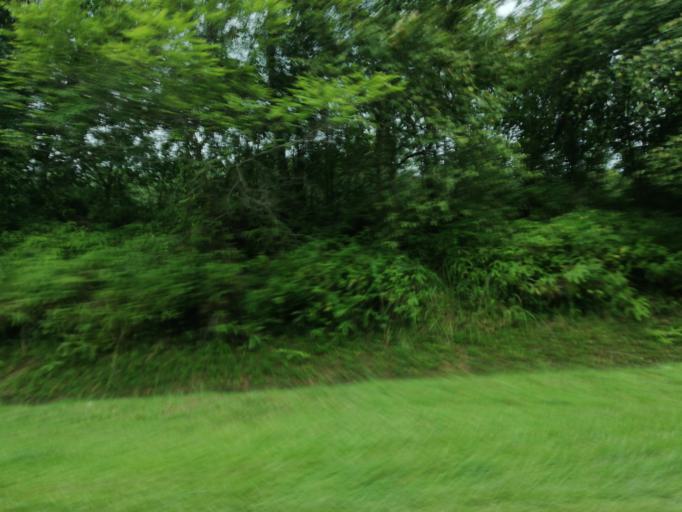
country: MY
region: Penang
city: Tasek Glugor
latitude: 5.4971
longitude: 100.6101
